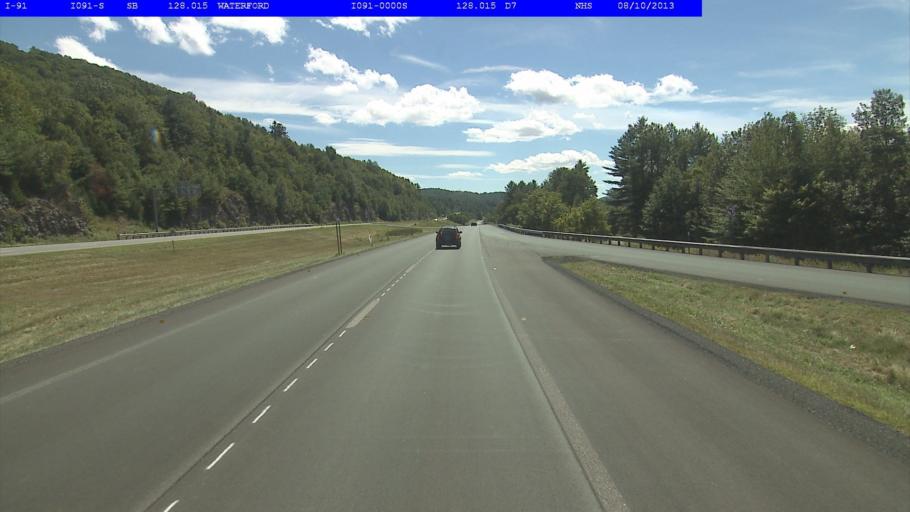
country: US
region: Vermont
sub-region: Caledonia County
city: Saint Johnsbury
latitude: 44.3931
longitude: -72.0175
